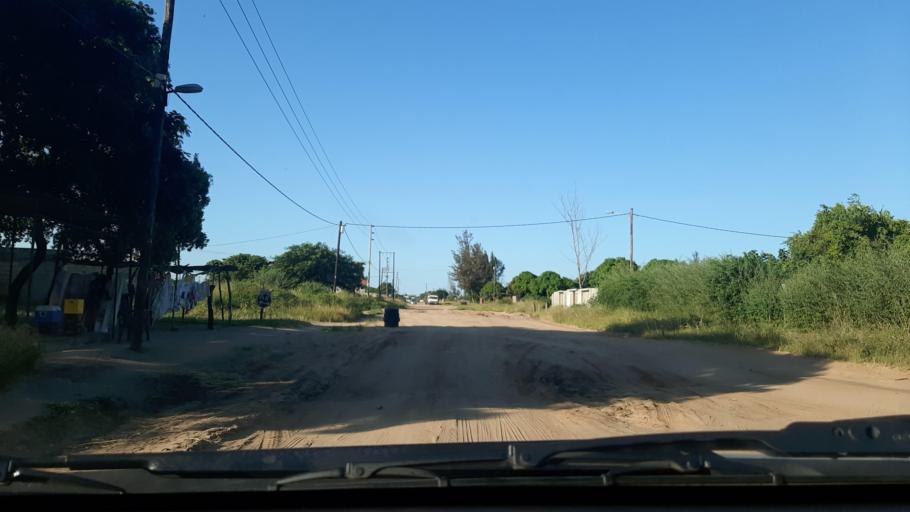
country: MZ
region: Maputo City
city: Maputo
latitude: -25.7616
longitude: 32.5483
